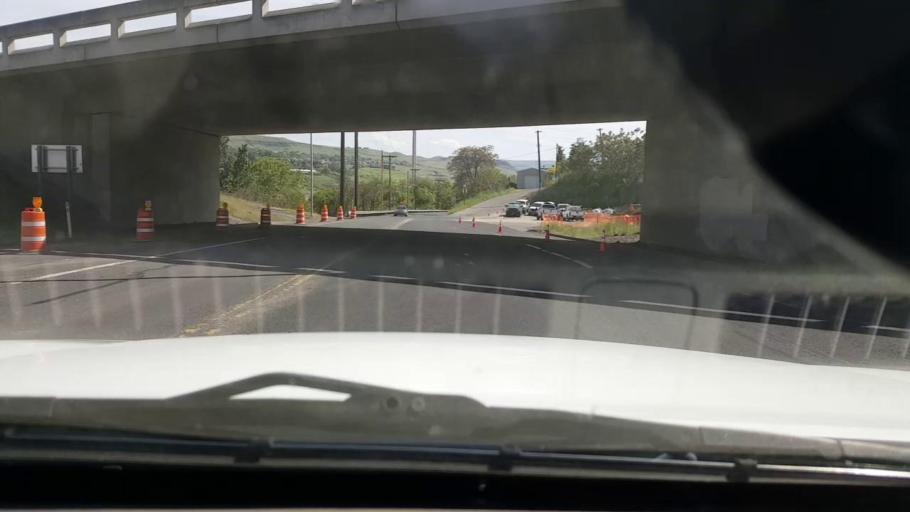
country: US
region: Washington
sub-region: Asotin County
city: Clarkston
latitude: 46.3974
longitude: -117.0443
